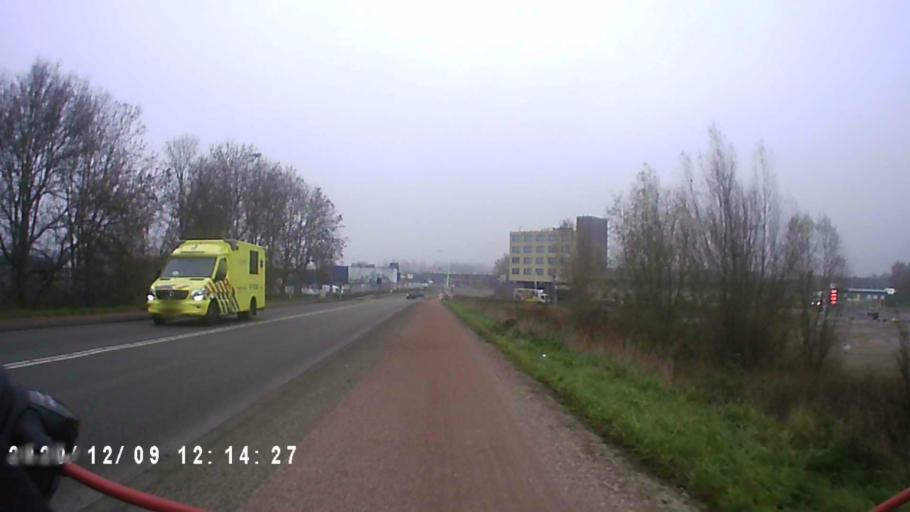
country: NL
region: Groningen
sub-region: Gemeente Haren
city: Haren
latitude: 53.2039
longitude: 6.6111
